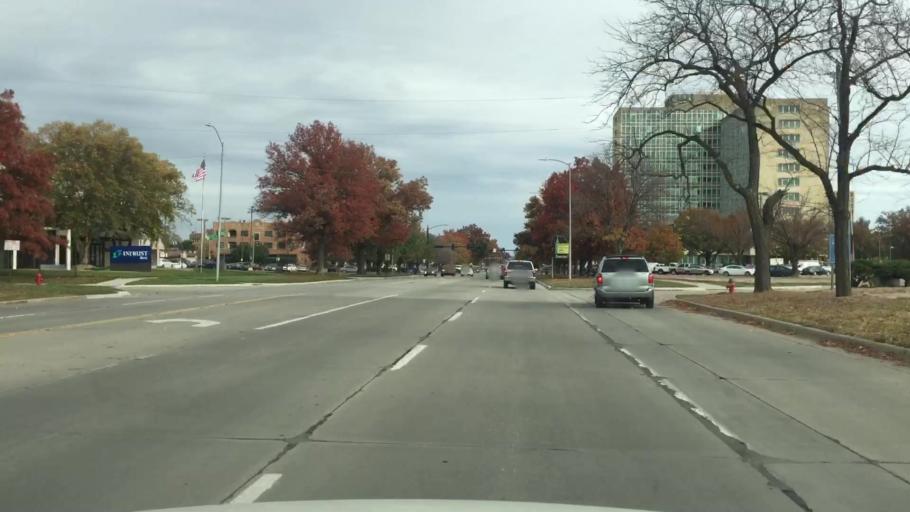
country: US
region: Kansas
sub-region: Shawnee County
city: Topeka
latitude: 39.0456
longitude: -95.6822
